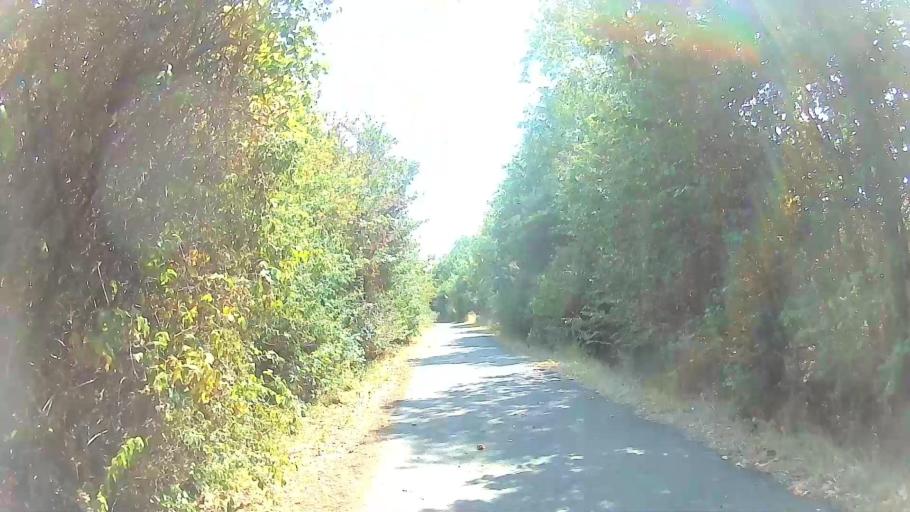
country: GB
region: England
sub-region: Greater London
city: Elm Park
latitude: 51.5324
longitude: 0.2055
